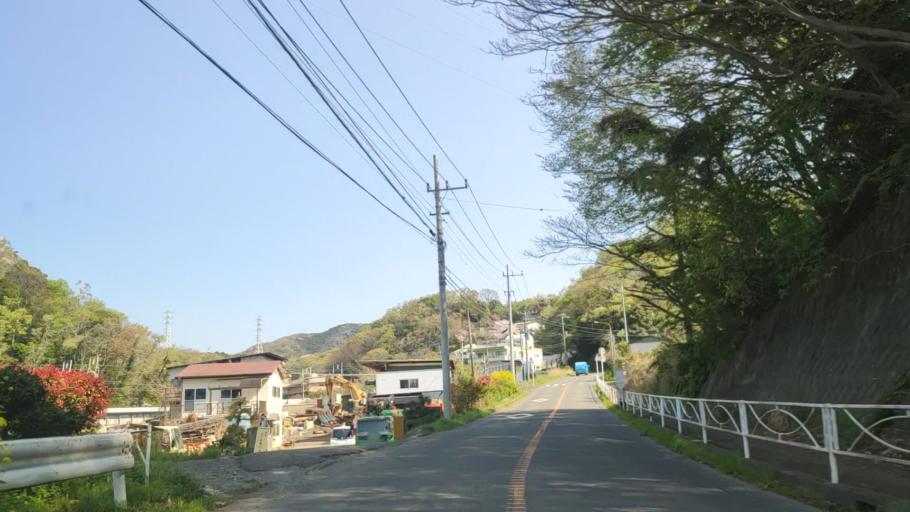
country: JP
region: Kanagawa
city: Ninomiya
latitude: 35.3134
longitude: 139.2724
